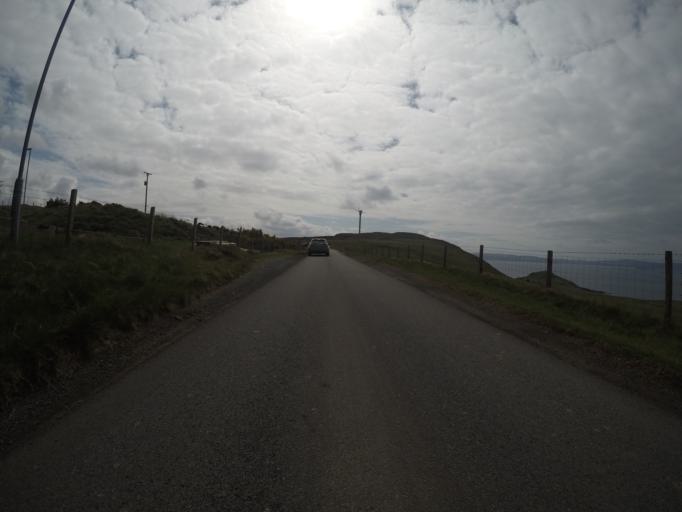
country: GB
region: Scotland
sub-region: Highland
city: Portree
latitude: 57.6029
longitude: -6.3776
